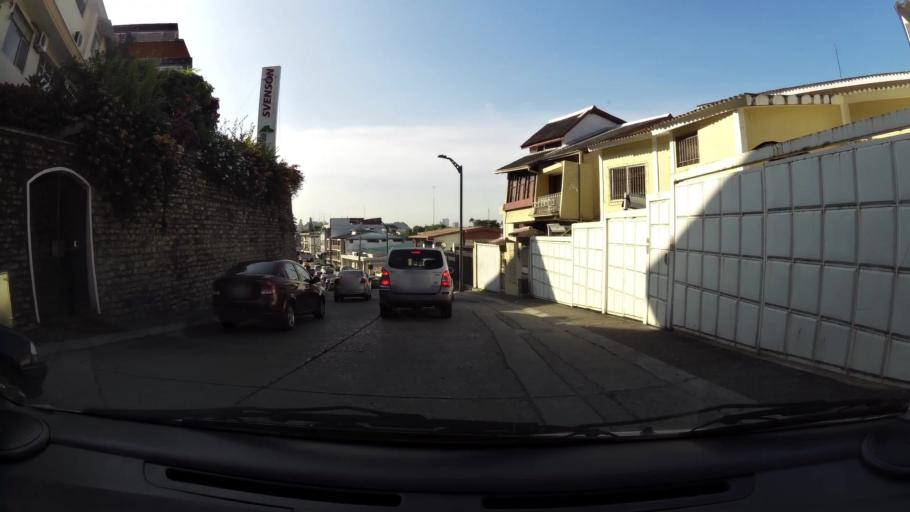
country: EC
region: Guayas
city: Guayaquil
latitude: -2.1664
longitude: -79.9061
